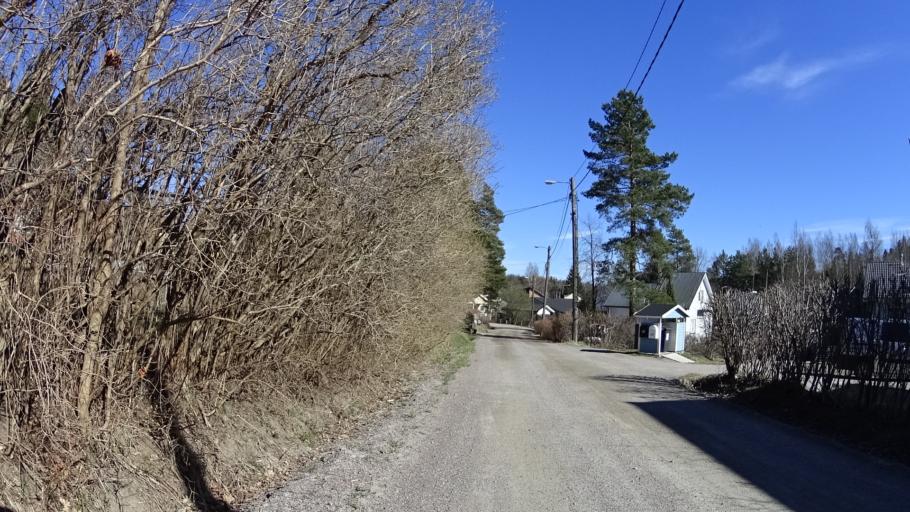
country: FI
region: Uusimaa
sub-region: Helsinki
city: Kilo
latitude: 60.2380
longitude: 24.7605
